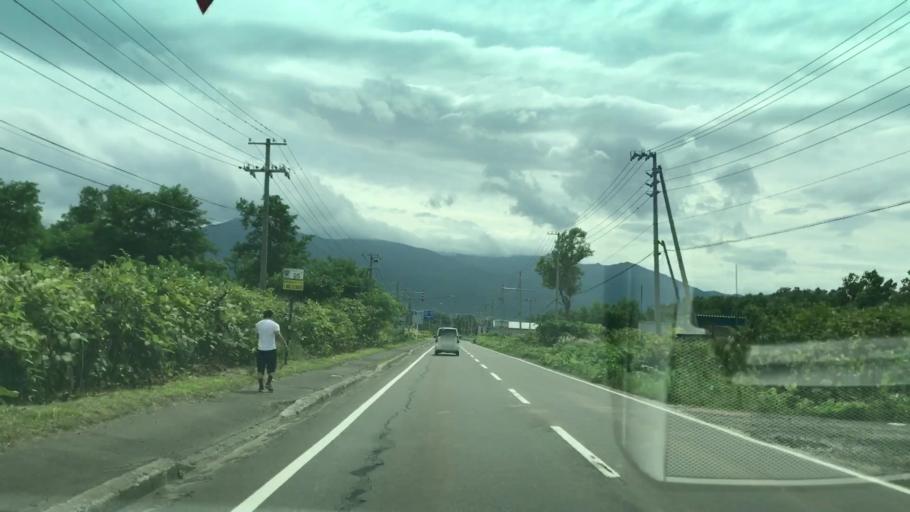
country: JP
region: Hokkaido
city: Iwanai
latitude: 43.0008
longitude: 140.5400
